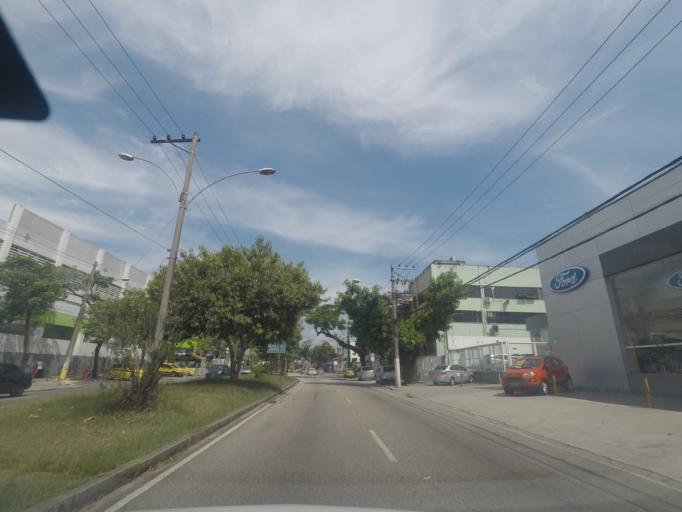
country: BR
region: Rio de Janeiro
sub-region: Rio De Janeiro
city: Rio de Janeiro
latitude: -22.8057
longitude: -43.2008
